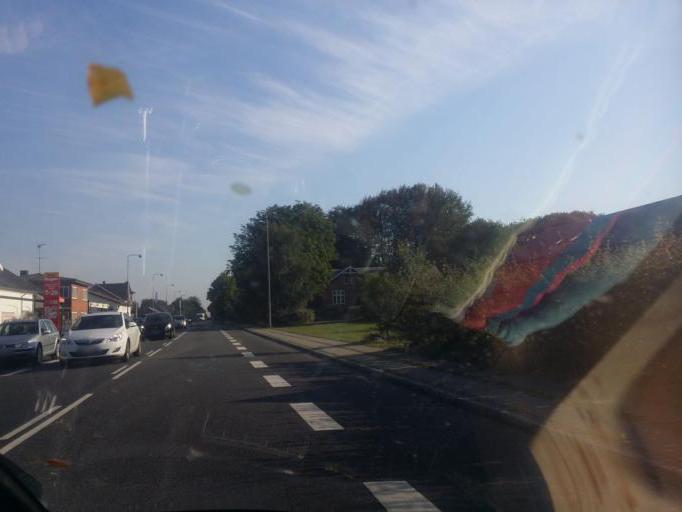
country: DK
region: South Denmark
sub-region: Esbjerg Kommune
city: Ribe
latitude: 55.2755
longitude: 8.7290
